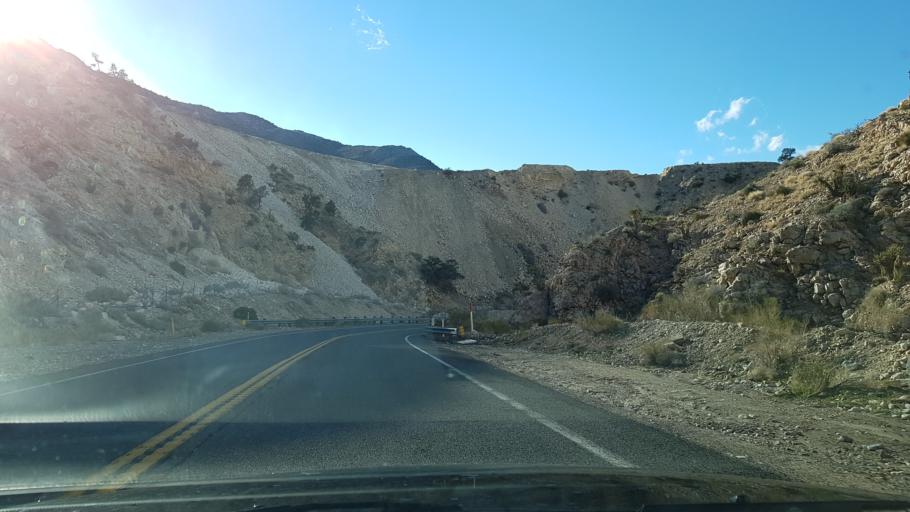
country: US
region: California
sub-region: San Bernardino County
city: Big Bear City
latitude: 34.3476
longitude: -116.8447
